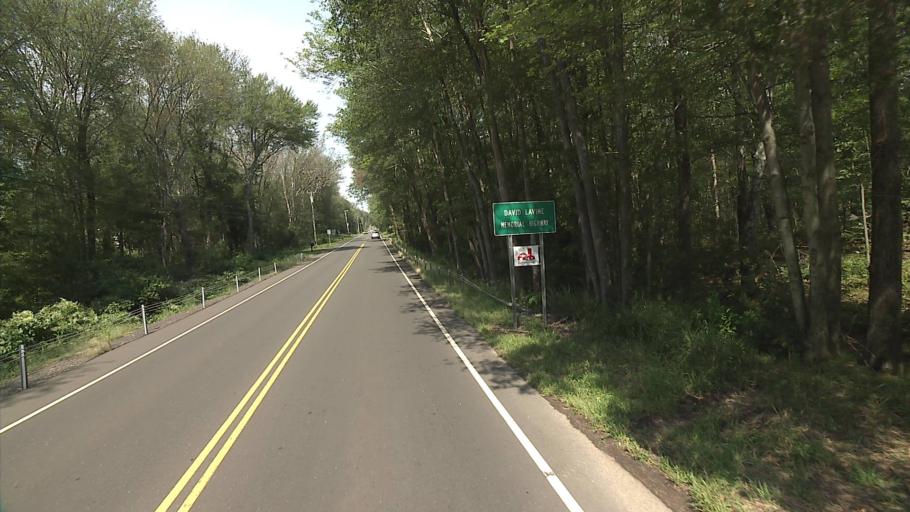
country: US
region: Connecticut
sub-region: Middlesex County
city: Durham
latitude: 41.4387
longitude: -72.6538
